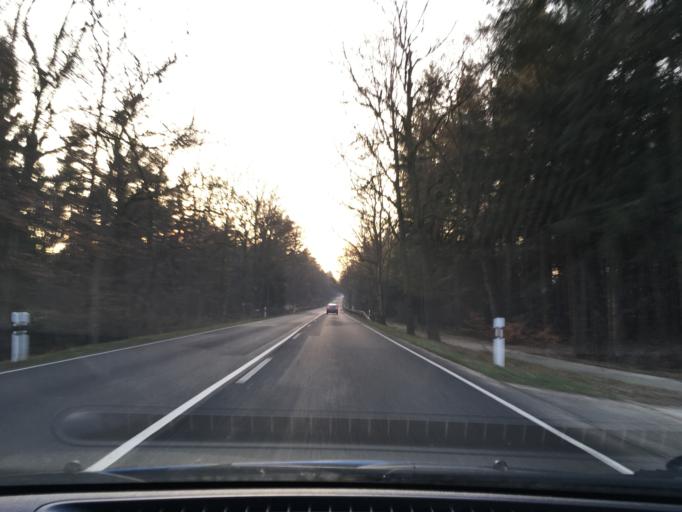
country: DE
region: Lower Saxony
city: Unterluss
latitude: 52.7770
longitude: 10.3333
